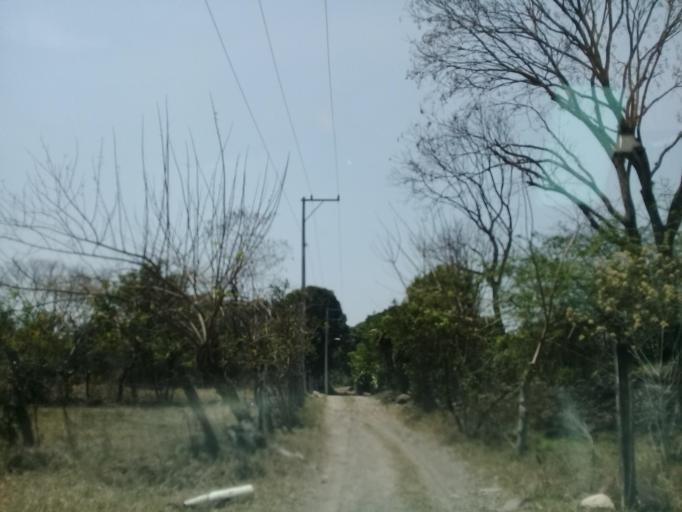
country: MX
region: Veracruz
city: Paraje Nuevo
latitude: 18.8713
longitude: -96.8668
